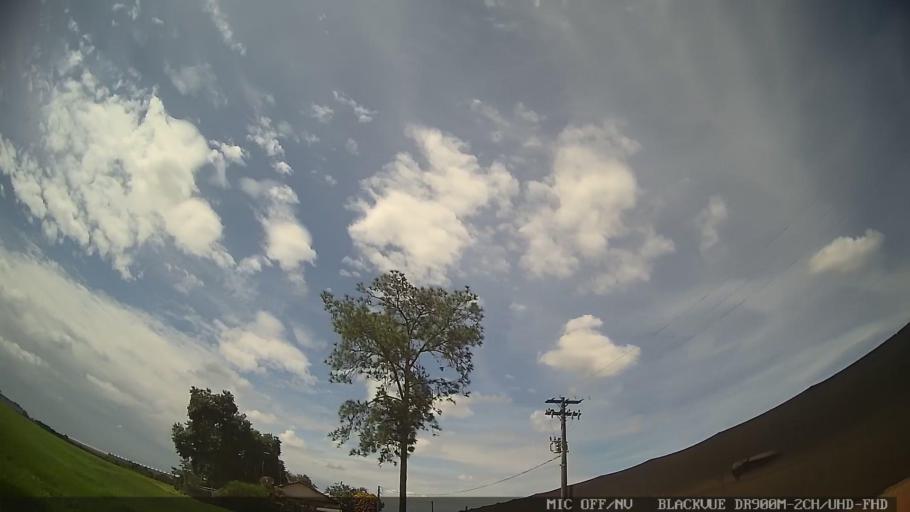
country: BR
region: Sao Paulo
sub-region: Artur Nogueira
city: Artur Nogueira
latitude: -22.6090
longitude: -47.0631
